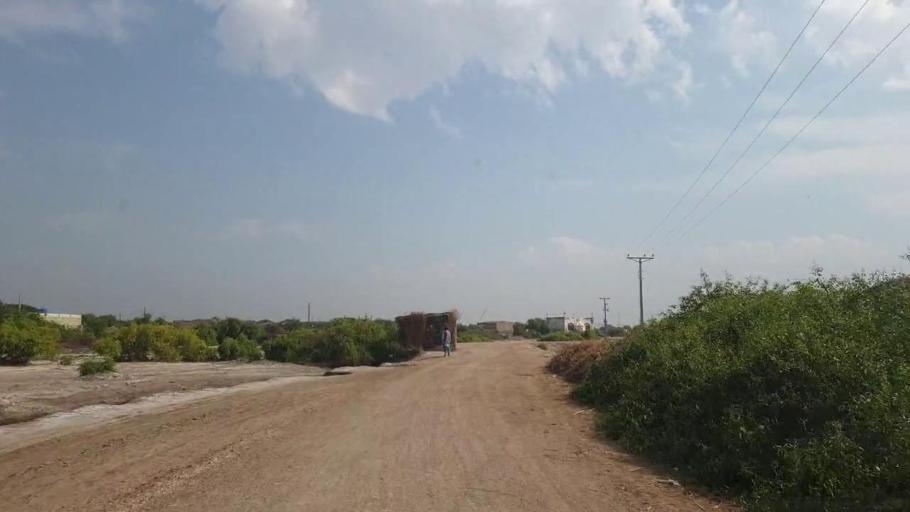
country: PK
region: Sindh
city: Tando Bago
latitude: 24.9030
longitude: 69.0529
